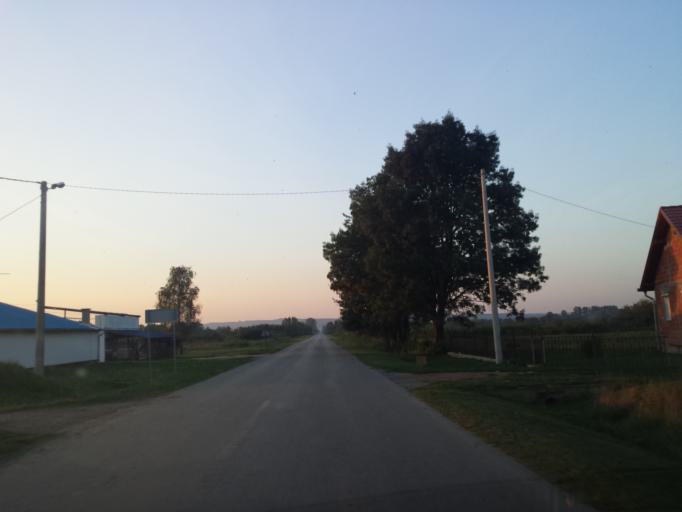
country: HR
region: Brodsko-Posavska
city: Oriovac
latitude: 45.1245
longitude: 17.8241
